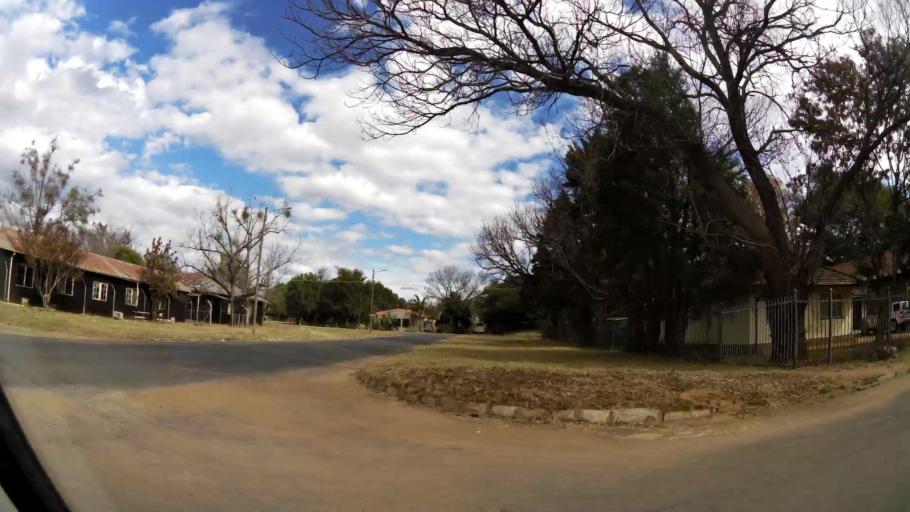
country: ZA
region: Limpopo
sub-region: Waterberg District Municipality
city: Modimolle
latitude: -24.7075
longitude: 28.4098
